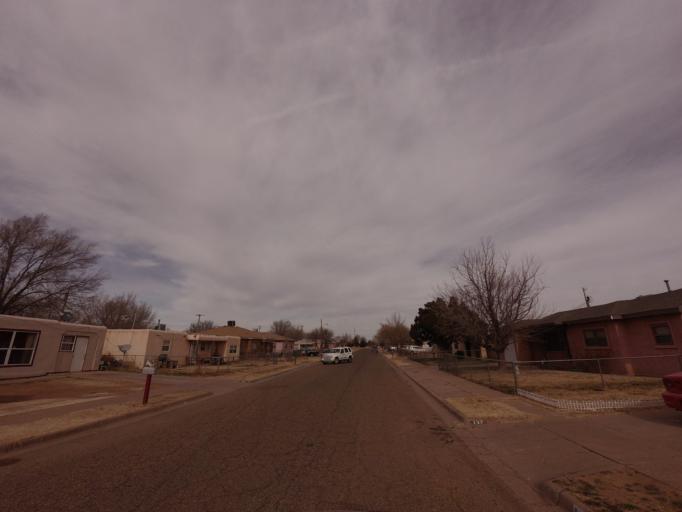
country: US
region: New Mexico
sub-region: Curry County
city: Clovis
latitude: 34.4029
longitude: -103.2410
